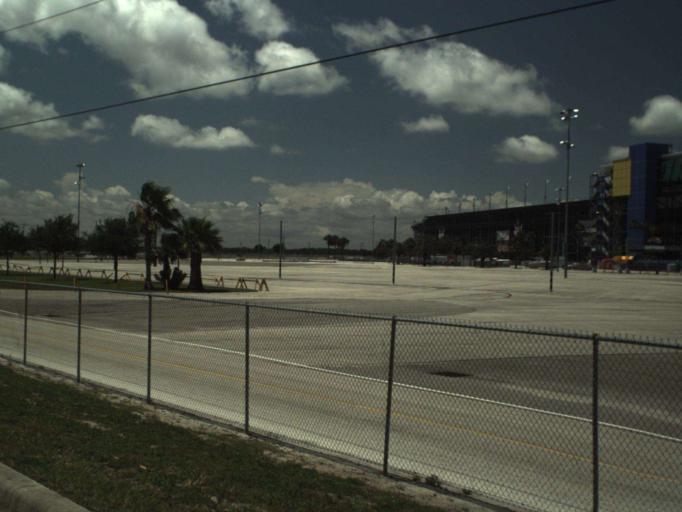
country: US
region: Florida
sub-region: Volusia County
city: Daytona Beach
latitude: 29.1832
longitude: -81.0631
